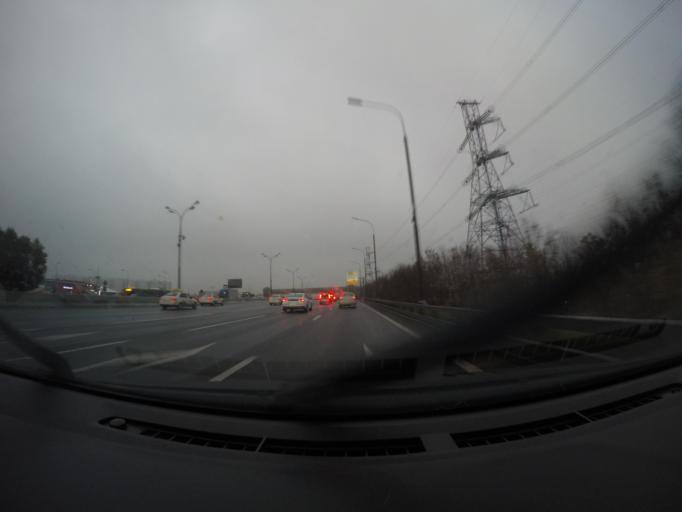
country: RU
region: Moscow
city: Annino
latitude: 55.5772
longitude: 37.5880
